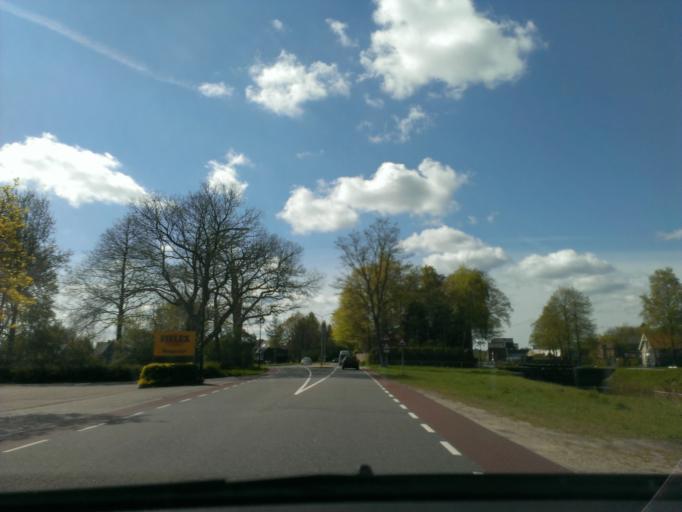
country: NL
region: Gelderland
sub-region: Gemeente Apeldoorn
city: Apeldoorn
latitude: 52.2219
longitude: 5.9736
